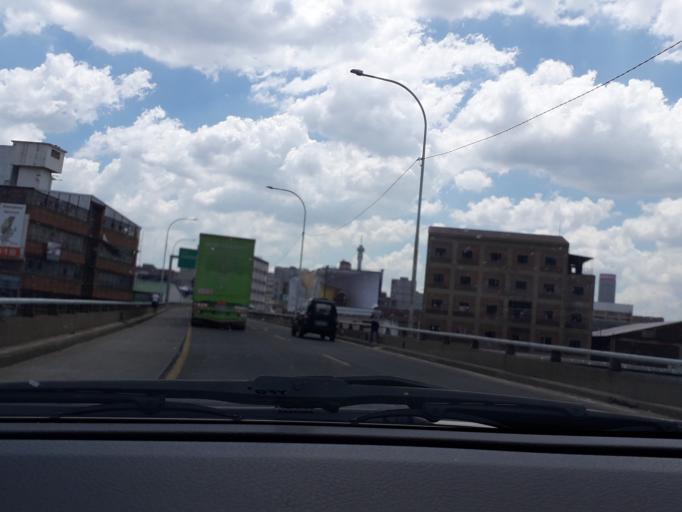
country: ZA
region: Gauteng
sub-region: City of Johannesburg Metropolitan Municipality
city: Johannesburg
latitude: -26.2095
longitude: 28.0556
